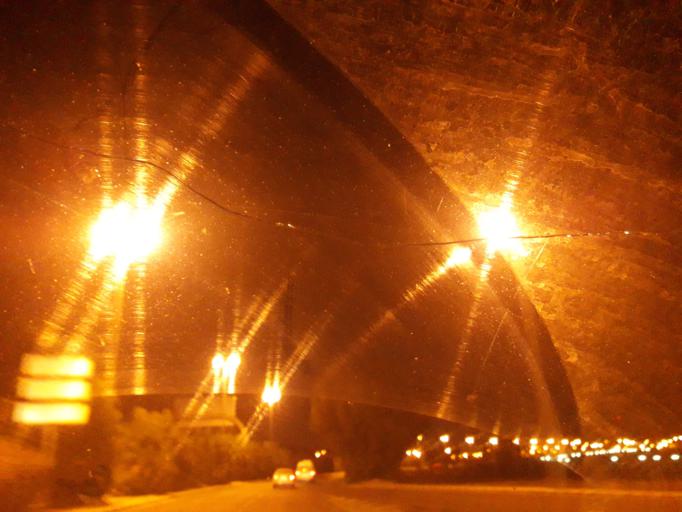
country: SA
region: Makkah
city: Ta'if
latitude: 21.3025
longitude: 40.3959
